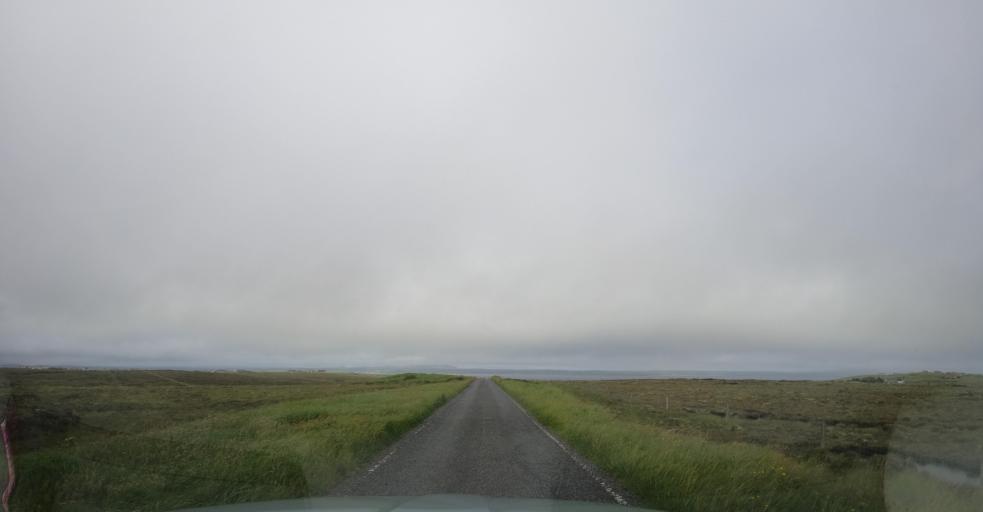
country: GB
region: Scotland
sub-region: Eilean Siar
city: Stornoway
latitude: 58.2038
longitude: -6.2432
